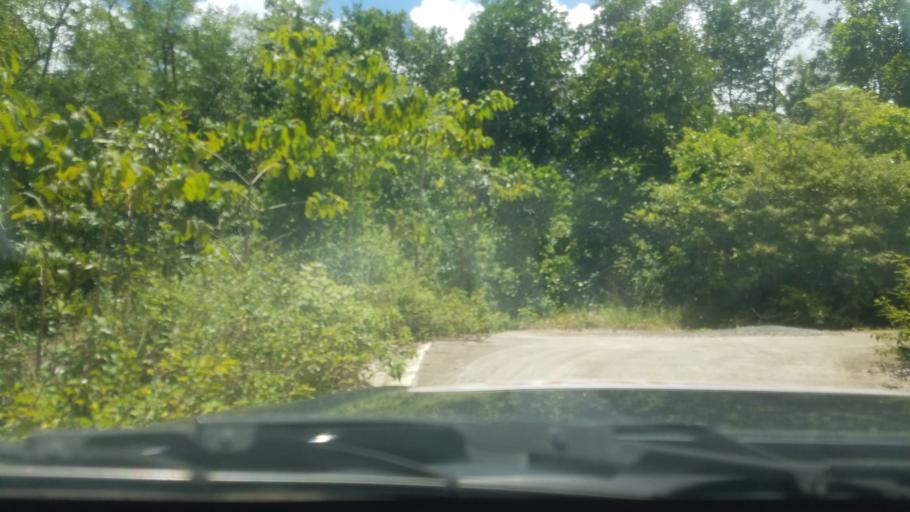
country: LC
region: Dennery Quarter
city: Dennery
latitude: 13.9197
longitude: -60.9032
